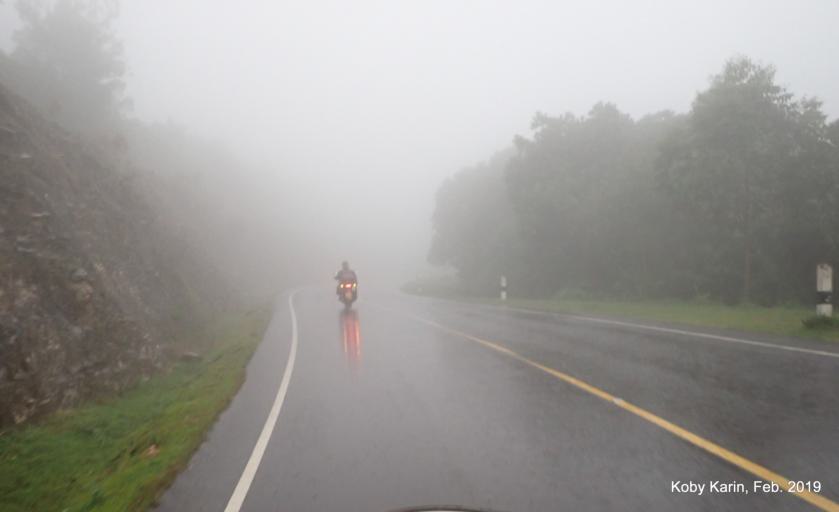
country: UG
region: Western Region
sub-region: Kisoro District
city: Kisoro
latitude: -1.2338
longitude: 29.8100
